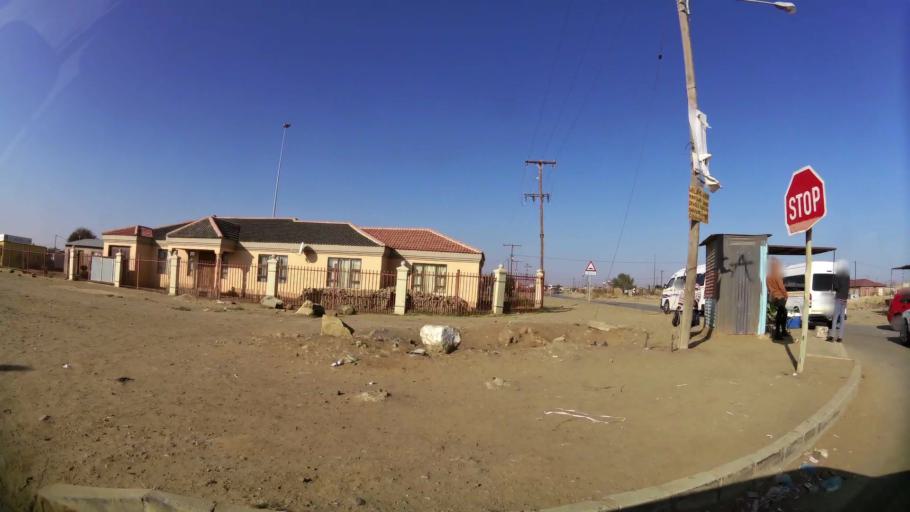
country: ZA
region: Orange Free State
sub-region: Mangaung Metropolitan Municipality
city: Bloemfontein
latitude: -29.2033
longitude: 26.2352
